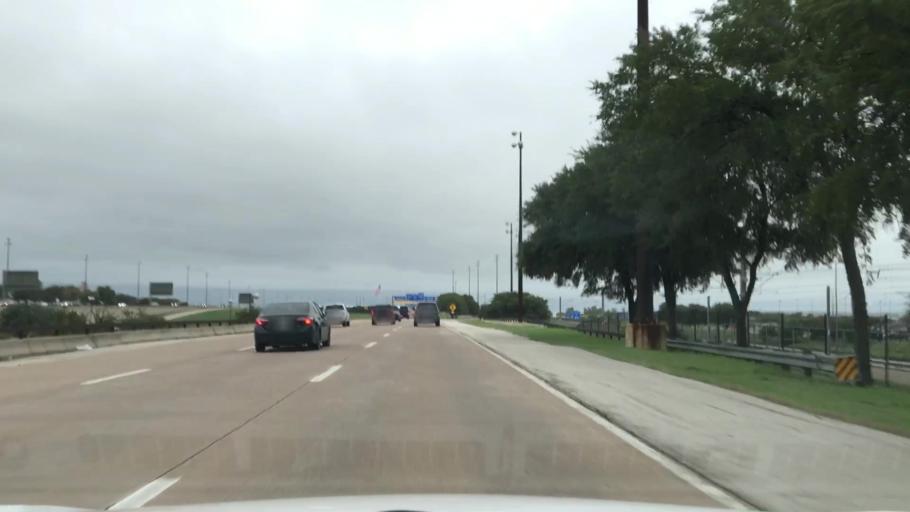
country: US
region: Texas
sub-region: Tarrant County
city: Grapevine
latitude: 32.9130
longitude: -97.0397
